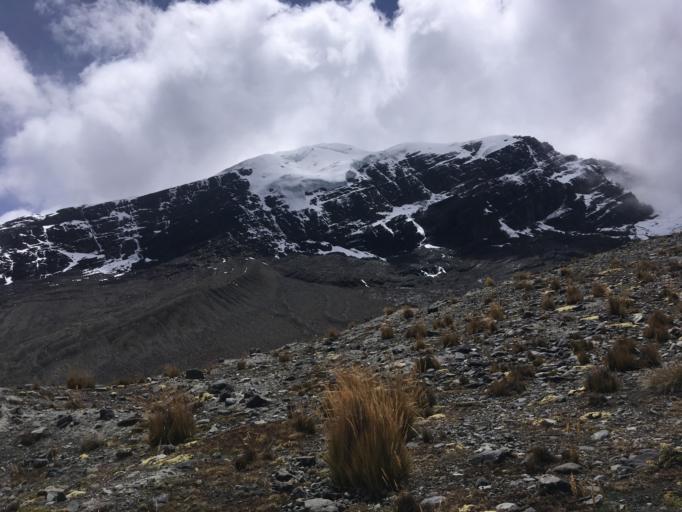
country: BO
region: La Paz
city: La Paz
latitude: -16.3969
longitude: -67.9535
